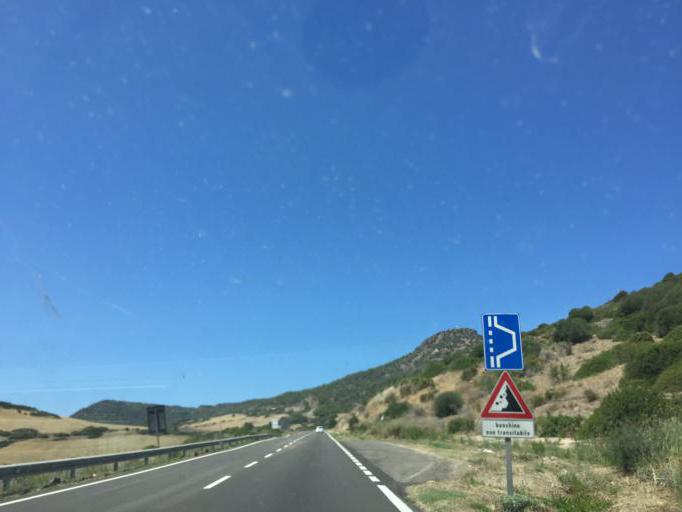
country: IT
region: Sardinia
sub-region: Provincia di Sassari
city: Valledoria
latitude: 40.9024
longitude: 8.7832
